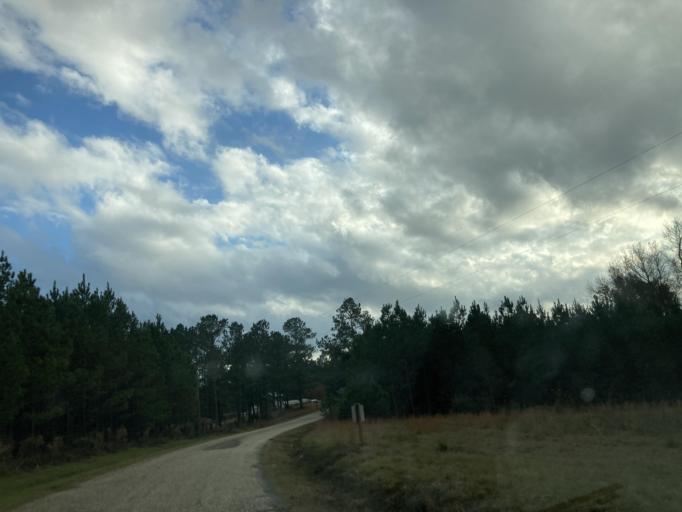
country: US
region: Mississippi
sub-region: Marion County
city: Columbia
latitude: 31.1766
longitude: -89.6639
